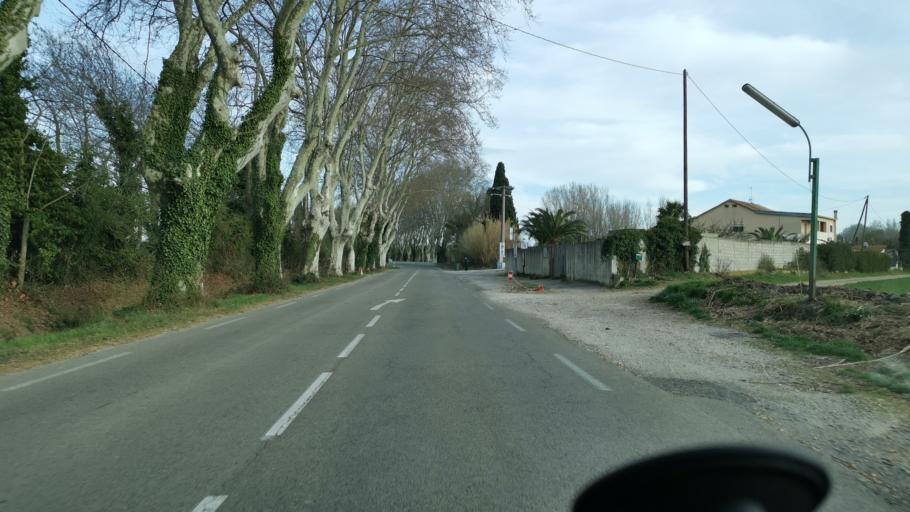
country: FR
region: Provence-Alpes-Cote d'Azur
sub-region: Departement des Bouches-du-Rhone
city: Saint-Martin-de-Crau
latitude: 43.6394
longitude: 4.7396
